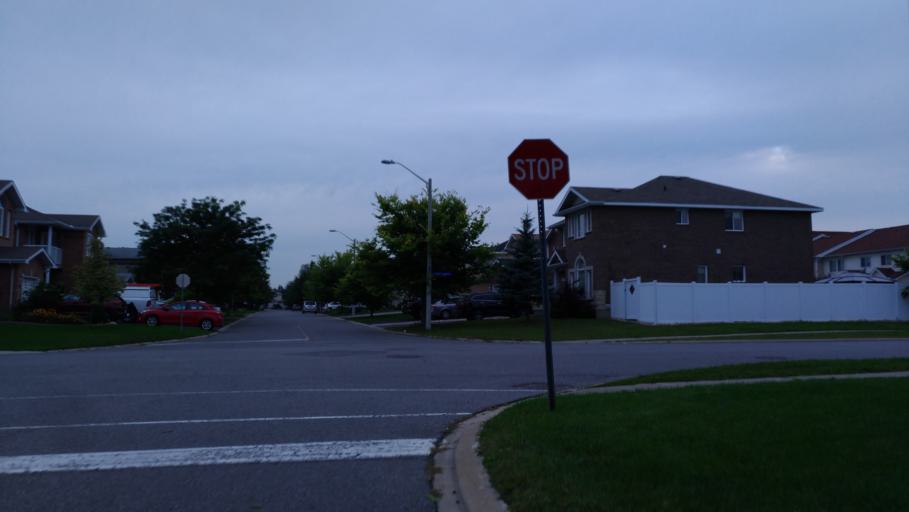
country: CA
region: Ontario
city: Bells Corners
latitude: 45.3555
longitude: -75.9371
